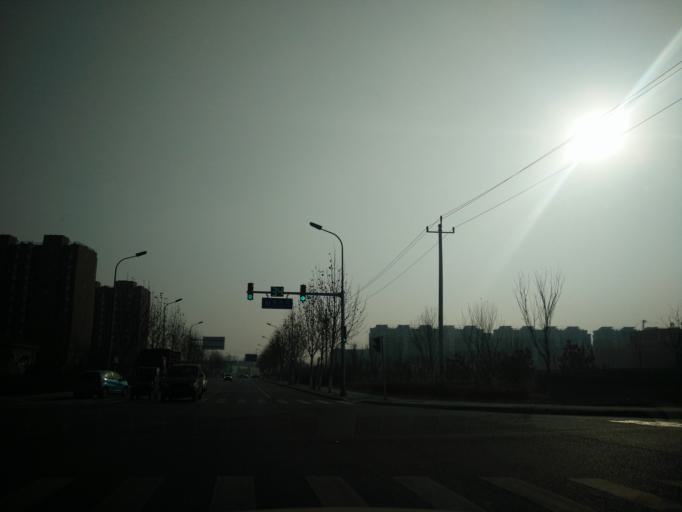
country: CN
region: Beijing
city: Yinghai
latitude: 39.7107
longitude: 116.3975
